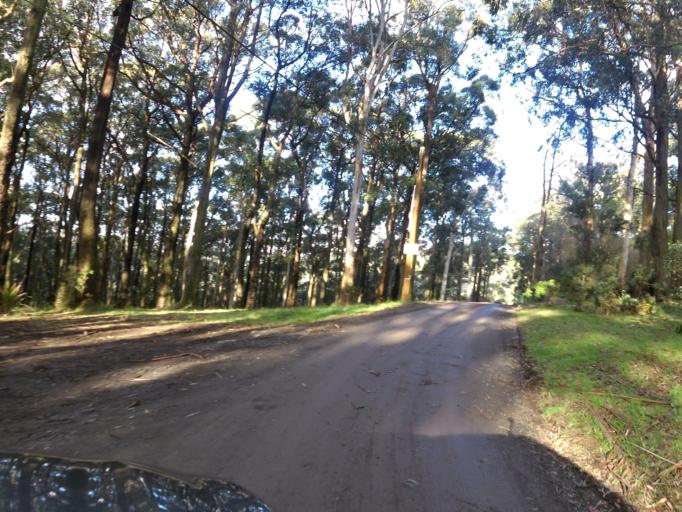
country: AU
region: Victoria
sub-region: Yarra Ranges
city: Ferny Creek
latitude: -37.8721
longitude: 145.3252
